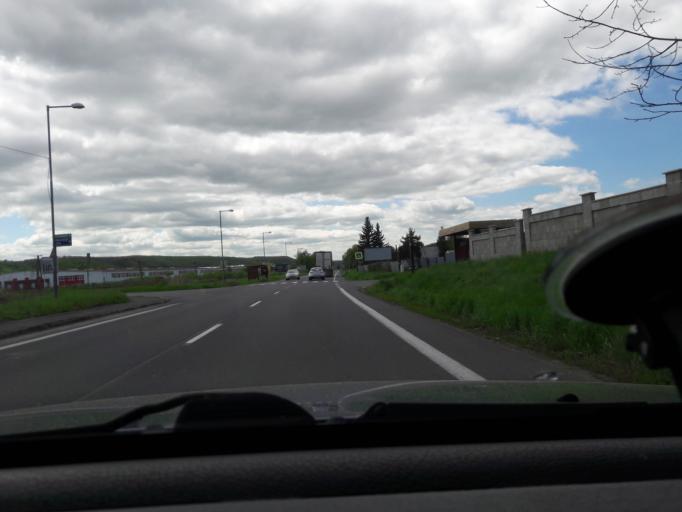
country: SK
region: Banskobystricky
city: Krupina
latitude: 48.3416
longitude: 19.0661
